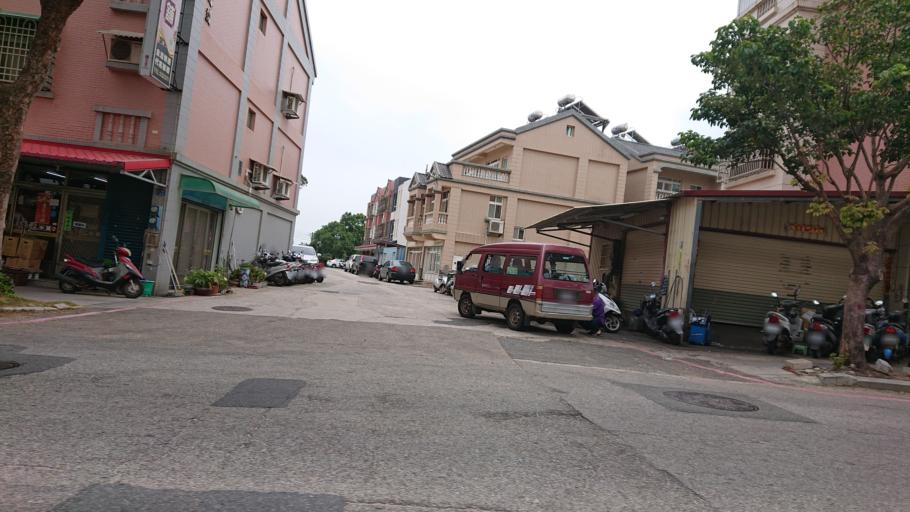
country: TW
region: Fukien
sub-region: Kinmen
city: Jincheng
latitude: 24.4370
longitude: 118.4106
